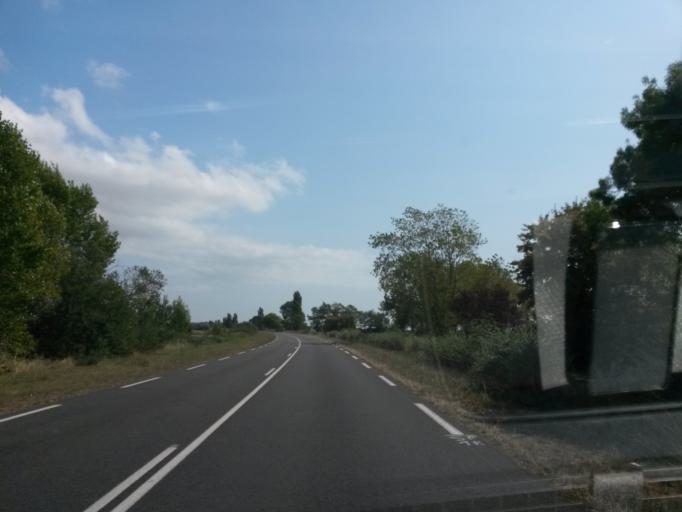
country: FR
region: Pays de la Loire
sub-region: Departement de la Vendee
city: La Tranche-sur-Mer
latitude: 46.3580
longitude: -1.4449
